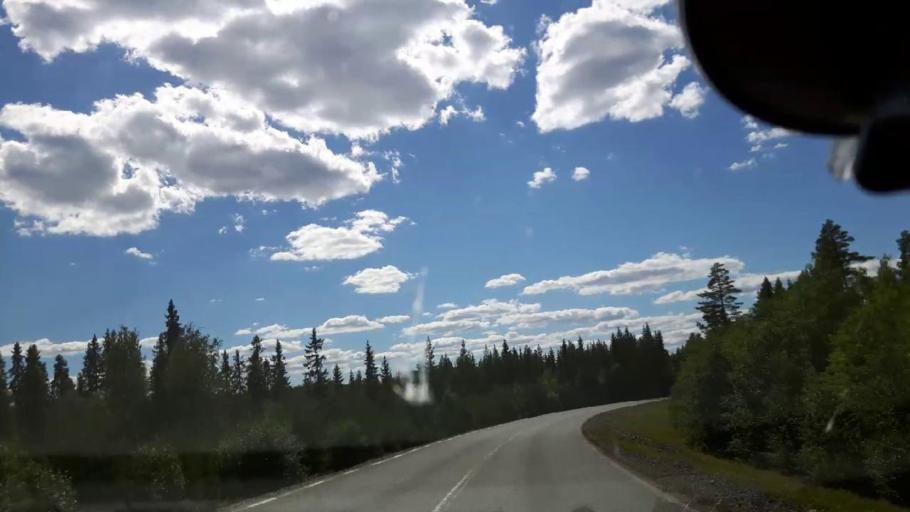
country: SE
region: Jaemtland
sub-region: Ragunda Kommun
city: Hammarstrand
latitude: 62.8605
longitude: 16.2132
